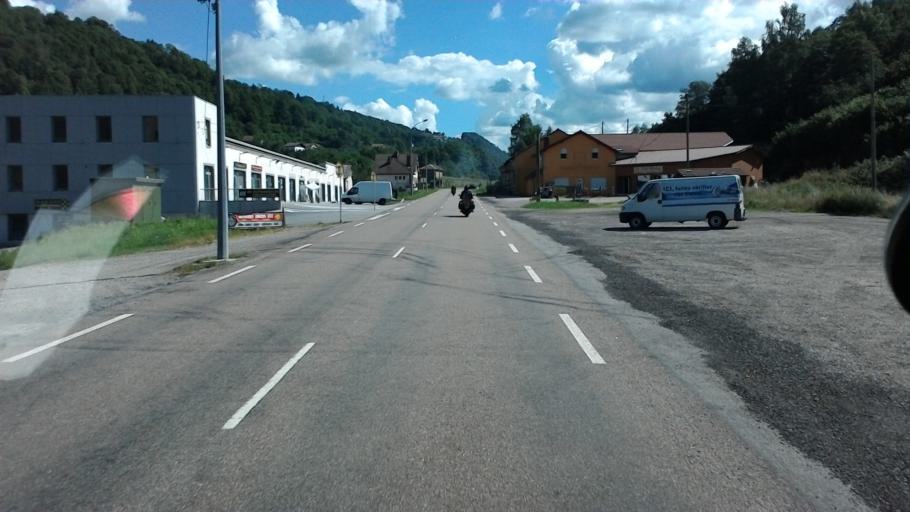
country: FR
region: Lorraine
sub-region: Departement des Vosges
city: La Bresse
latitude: 47.9872
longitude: 6.8406
